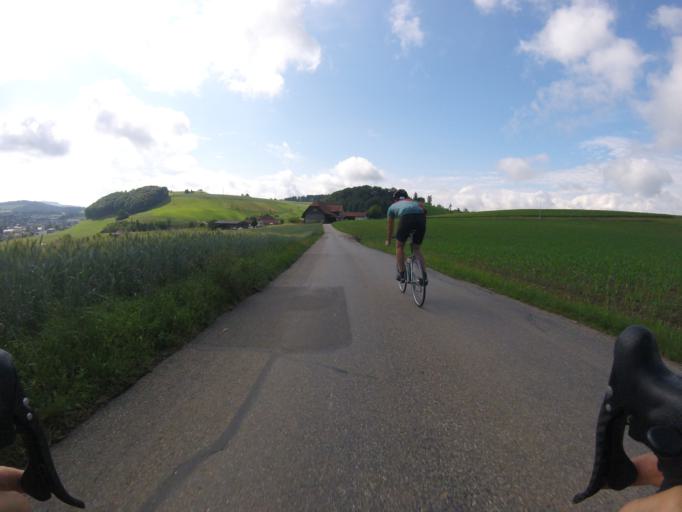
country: CH
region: Bern
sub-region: Bern-Mittelland District
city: Worb
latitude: 46.9298
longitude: 7.5475
